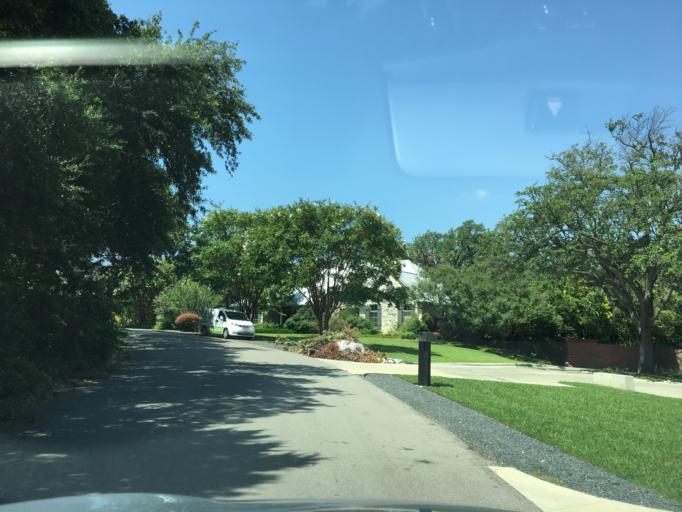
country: US
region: Texas
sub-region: Dallas County
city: University Park
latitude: 32.9070
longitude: -96.7831
